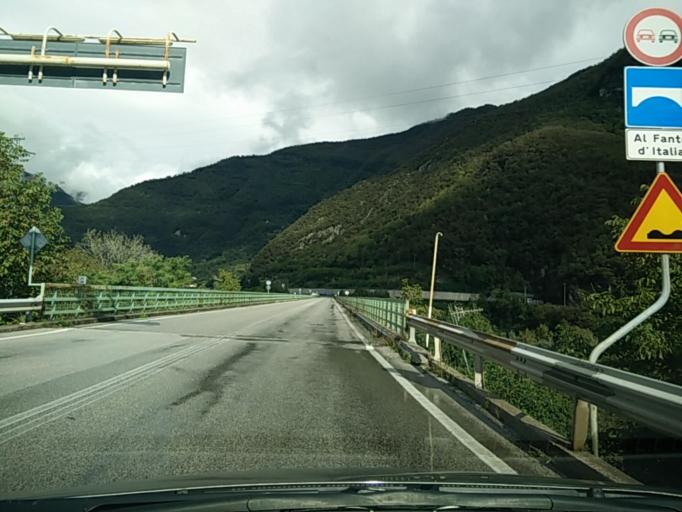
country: IT
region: Veneto
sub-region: Provincia di Belluno
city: Quero
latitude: 45.9272
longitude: 11.9406
